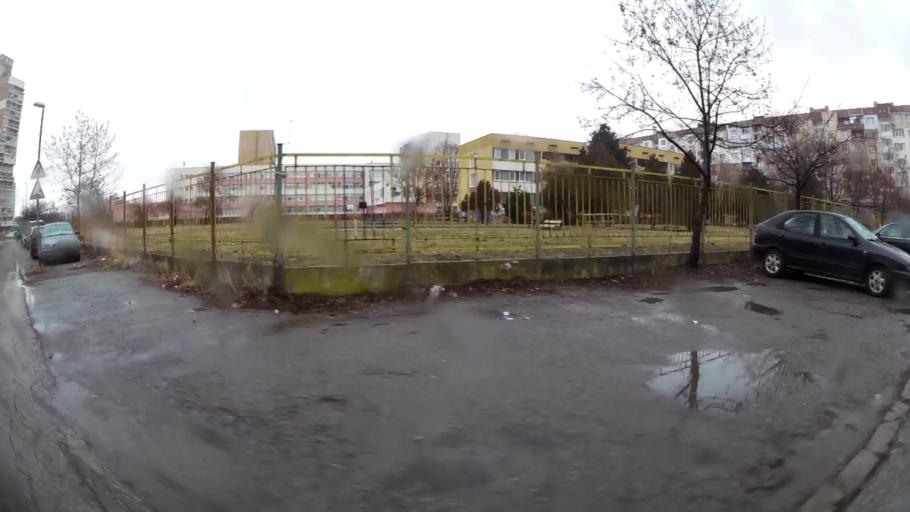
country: BG
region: Sofia-Capital
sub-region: Stolichna Obshtina
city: Sofia
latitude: 42.6595
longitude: 23.3979
